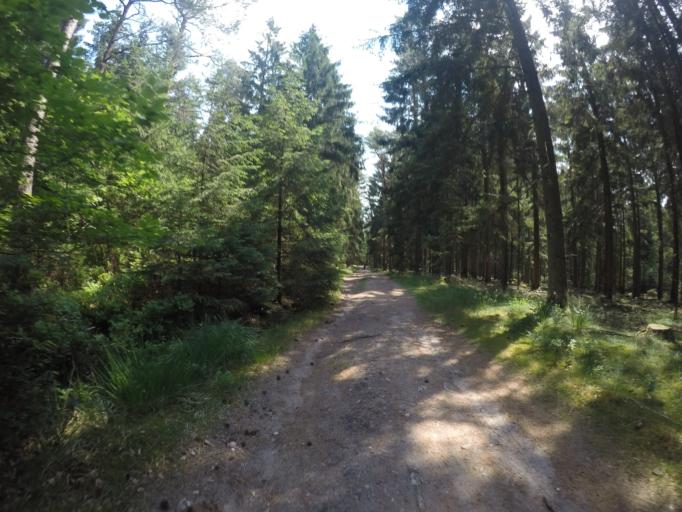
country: DE
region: Lower Saxony
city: Buchholz in der Nordheide
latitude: 53.2936
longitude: 9.8410
